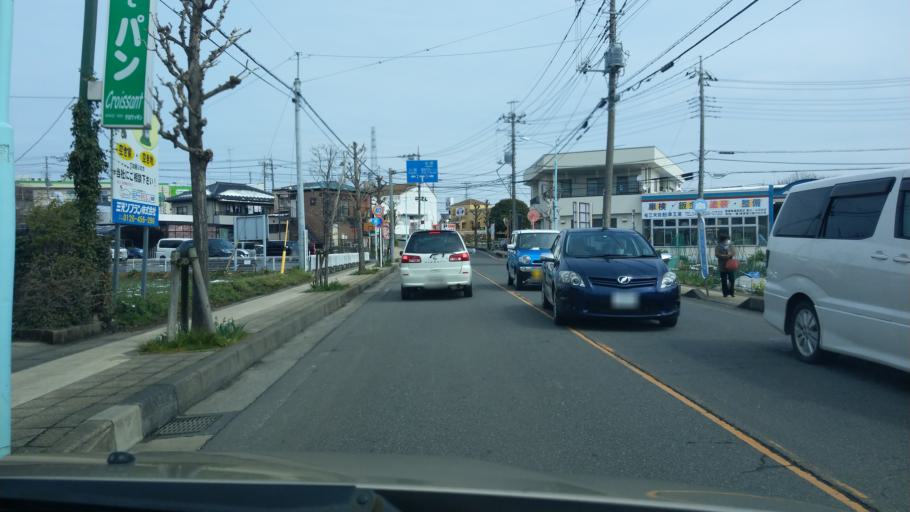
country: JP
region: Saitama
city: Yono
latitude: 35.9112
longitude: 139.5777
